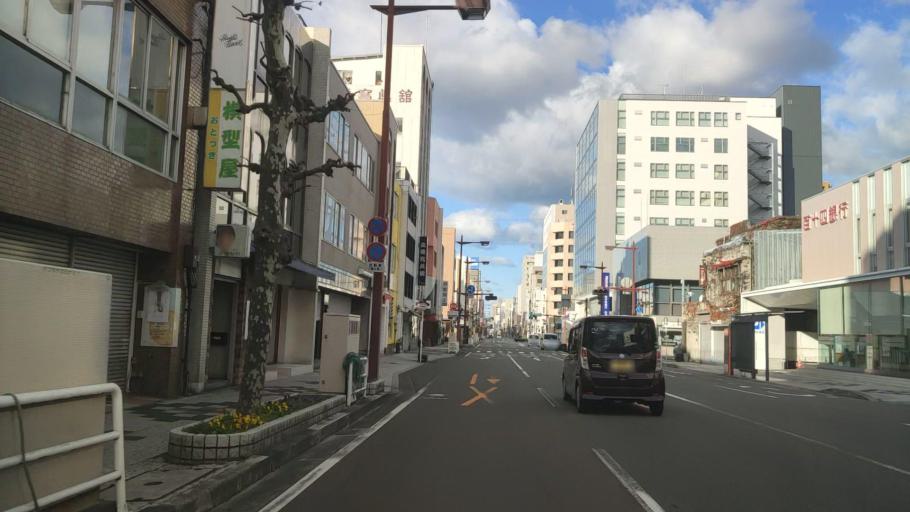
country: JP
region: Ehime
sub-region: Shikoku-chuo Shi
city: Matsuyama
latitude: 33.8366
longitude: 132.7697
